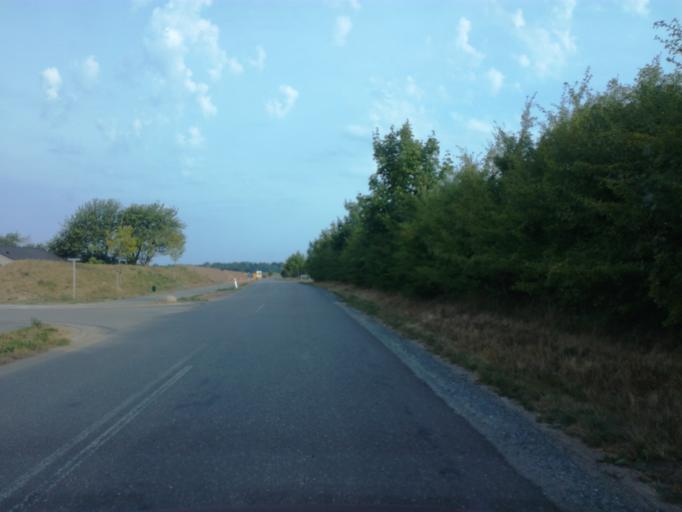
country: DK
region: South Denmark
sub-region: Vejle Kommune
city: Borkop
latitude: 55.6385
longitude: 9.6399
